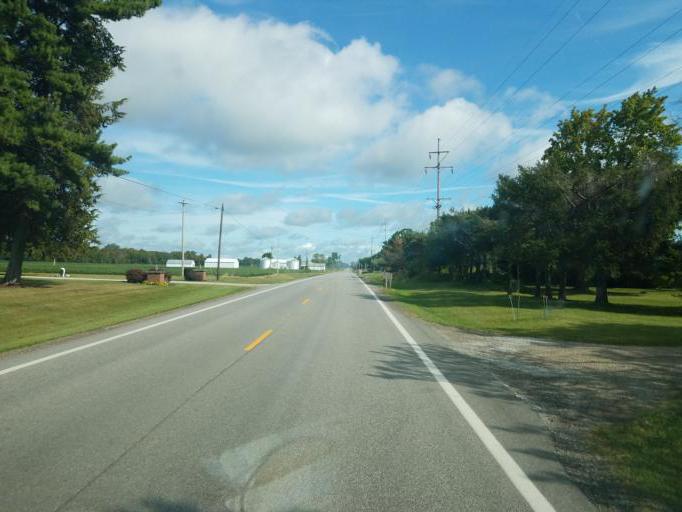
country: US
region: Ohio
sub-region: Wayne County
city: West Salem
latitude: 41.0717
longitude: -82.1238
